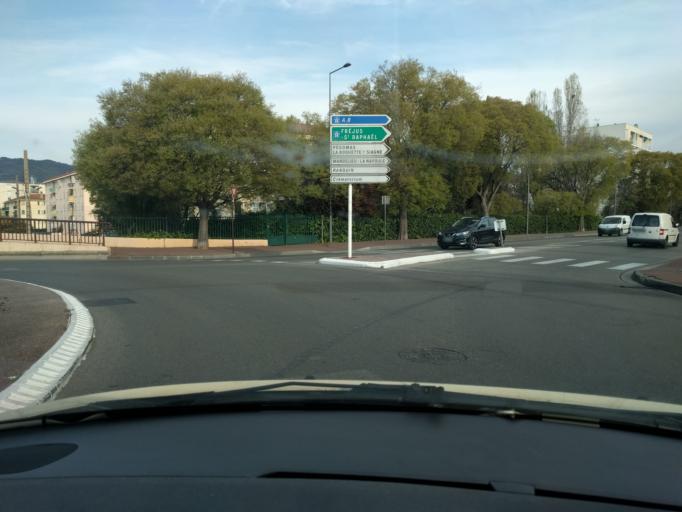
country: FR
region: Provence-Alpes-Cote d'Azur
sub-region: Departement des Alpes-Maritimes
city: Mandelieu-la-Napoule
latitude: 43.5572
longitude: 6.9688
